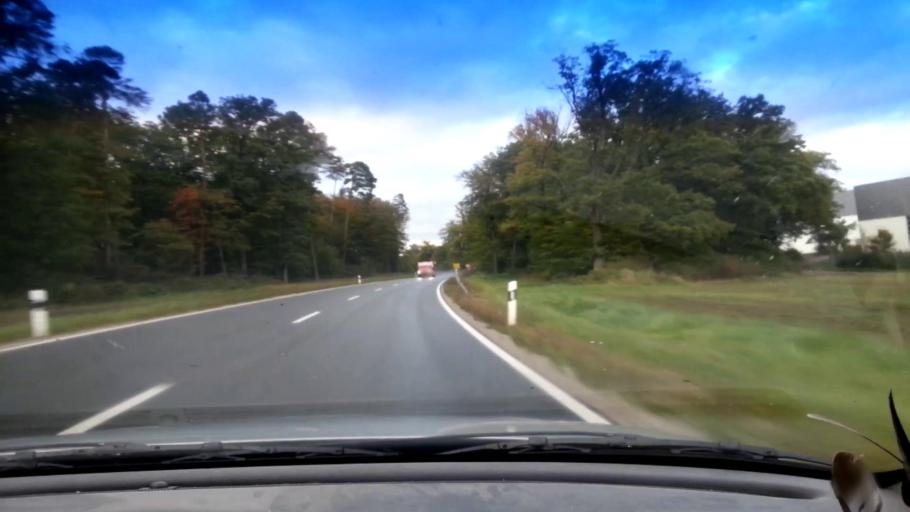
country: DE
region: Bavaria
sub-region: Upper Franconia
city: Burgebrach
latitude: 49.8045
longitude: 10.7284
